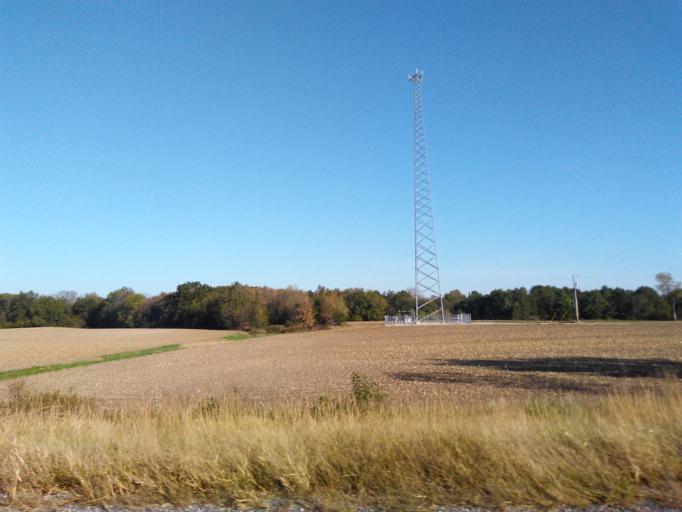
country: US
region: Illinois
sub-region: Madison County
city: Highland
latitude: 38.7849
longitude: -89.7265
